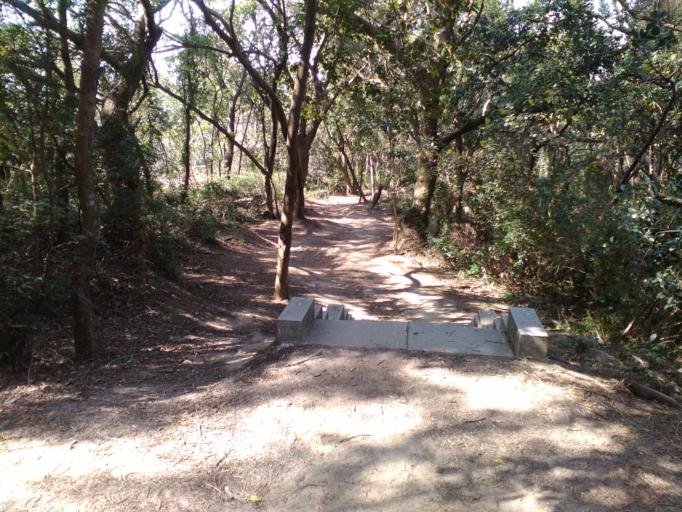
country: TW
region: Fukien
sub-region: Kinmen
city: Jincheng
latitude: 24.4633
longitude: 118.4104
